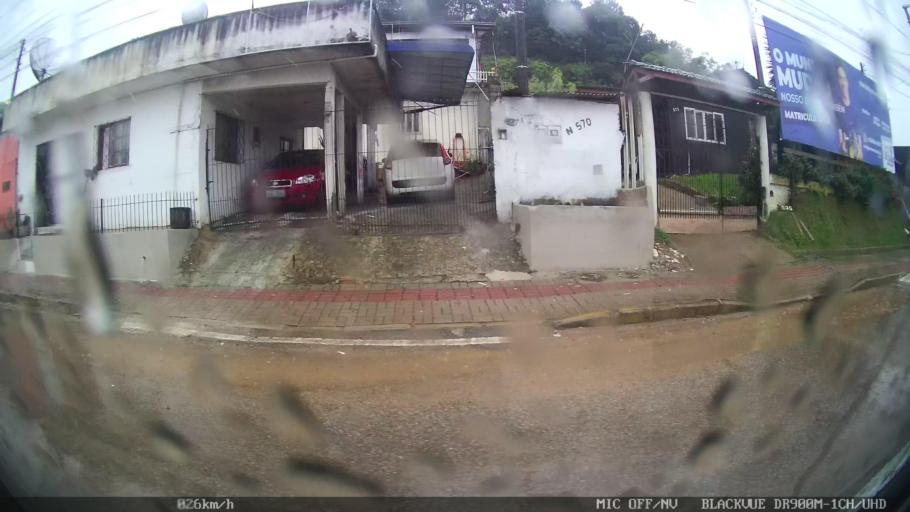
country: BR
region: Santa Catarina
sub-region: Balneario Camboriu
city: Balneario Camboriu
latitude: -27.0071
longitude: -48.6481
